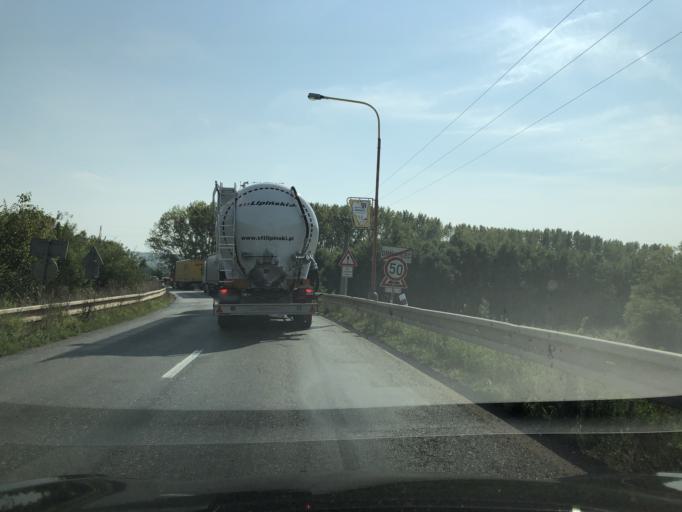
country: CZ
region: South Moravian
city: Drnholec
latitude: 48.8558
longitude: 16.4880
